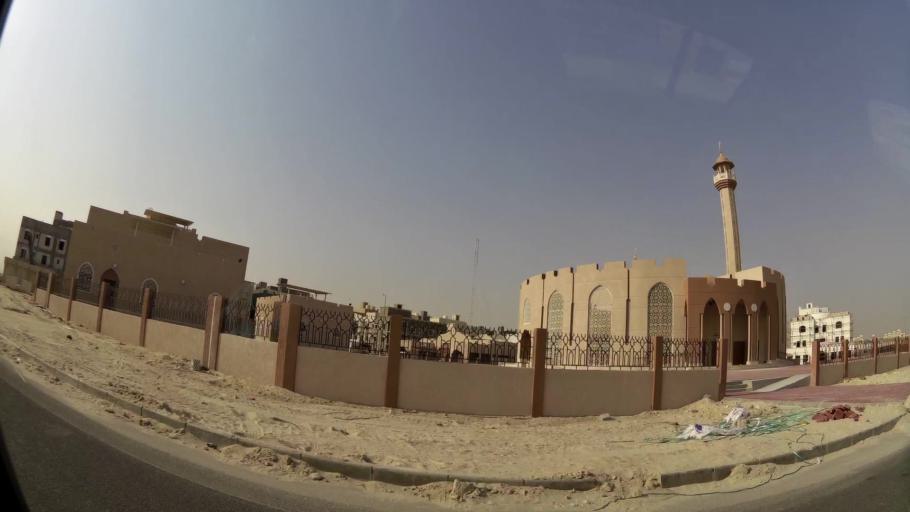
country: KW
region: Al Asimah
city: Ar Rabiyah
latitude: 29.3327
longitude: 47.8125
